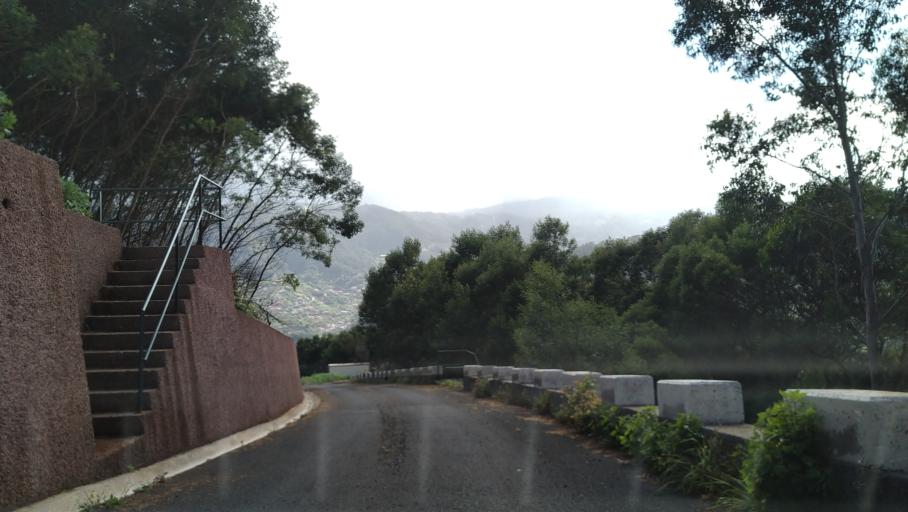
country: PT
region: Madeira
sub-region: Machico
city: Canical
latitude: 32.7423
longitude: -16.7700
